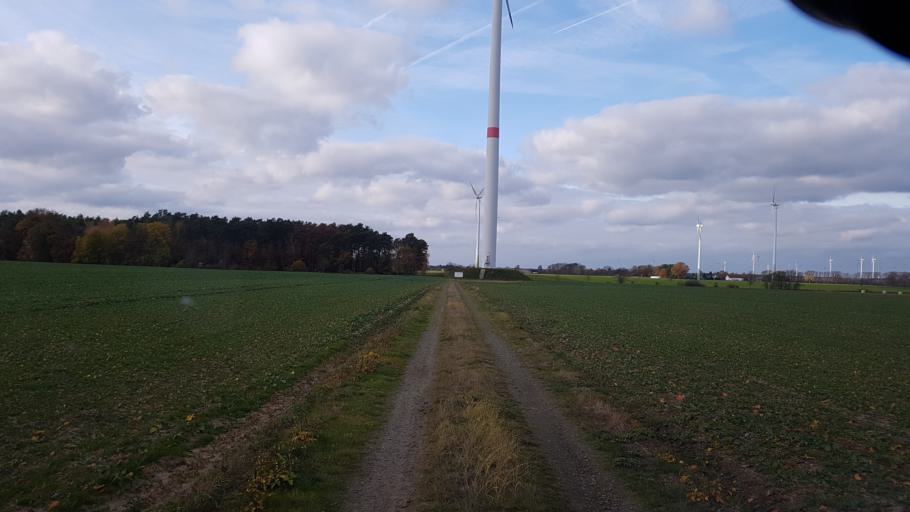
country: DE
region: Brandenburg
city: Sallgast
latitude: 51.6002
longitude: 13.8822
